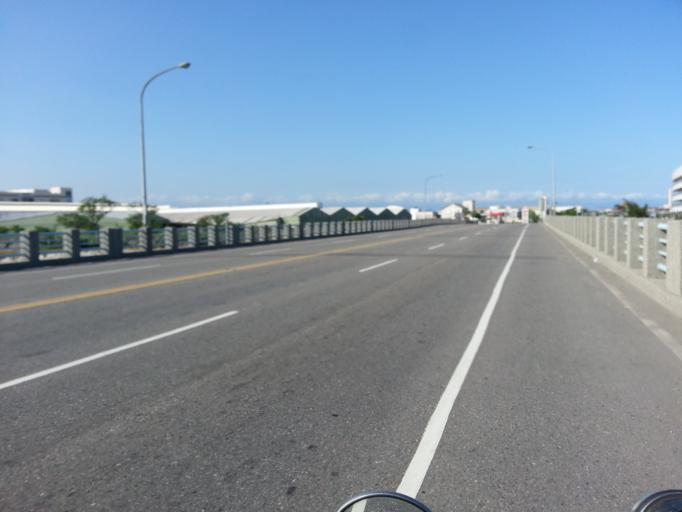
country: TW
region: Taiwan
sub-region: Yilan
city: Yilan
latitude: 24.6313
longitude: 121.8319
